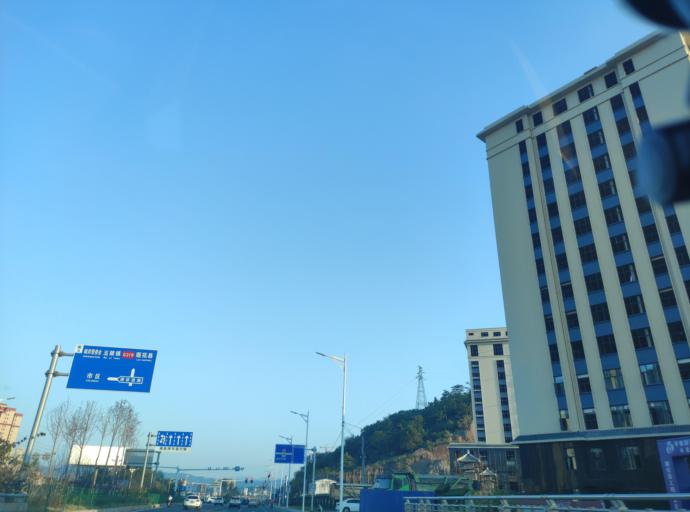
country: CN
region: Jiangxi Sheng
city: Pingxiang
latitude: 27.6444
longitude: 113.8250
